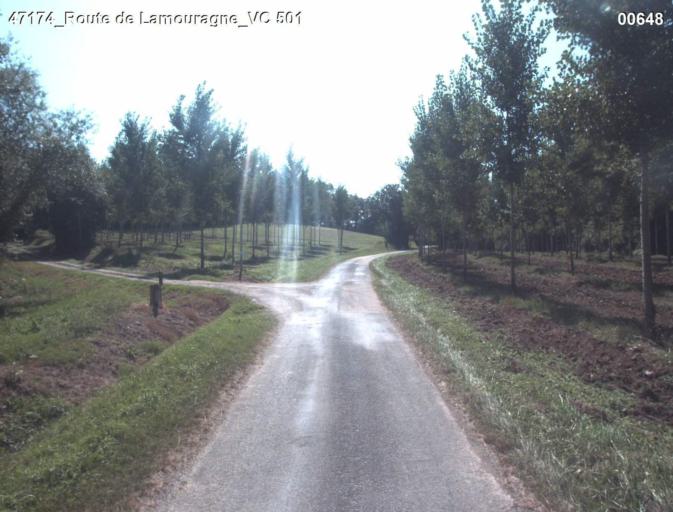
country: FR
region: Midi-Pyrenees
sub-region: Departement du Gers
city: Condom
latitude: 44.0419
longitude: 0.3863
